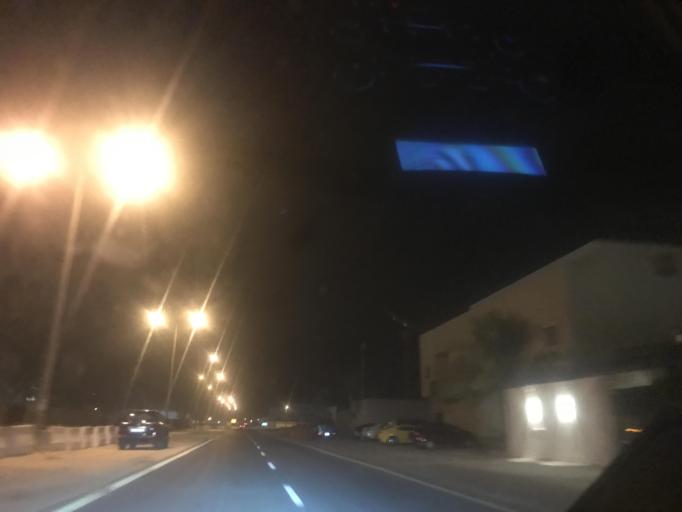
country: SA
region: Ar Riyad
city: Riyadh
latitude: 24.7651
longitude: 46.5931
